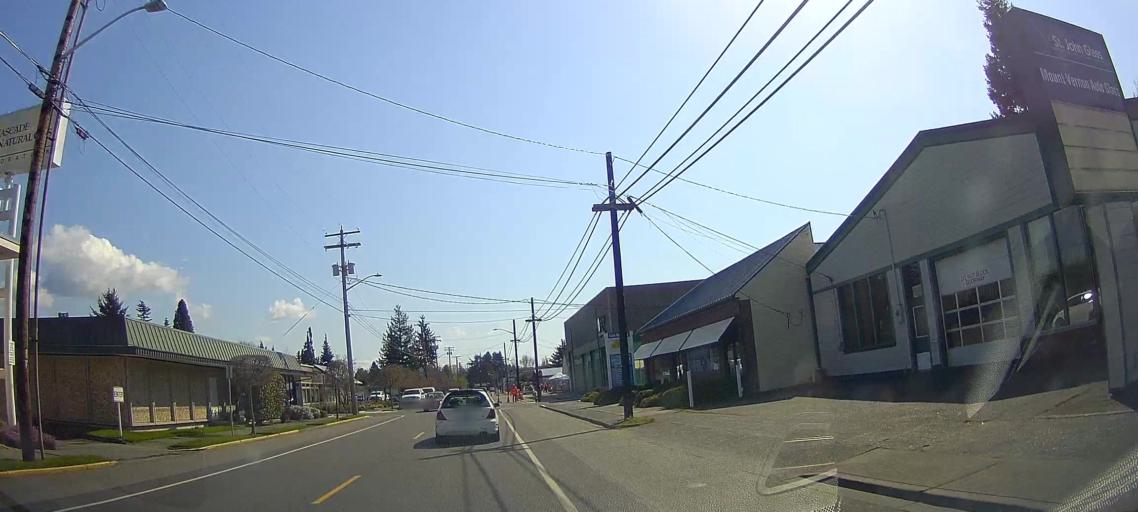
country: US
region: Washington
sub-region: Skagit County
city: Mount Vernon
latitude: 48.4109
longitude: -122.3379
